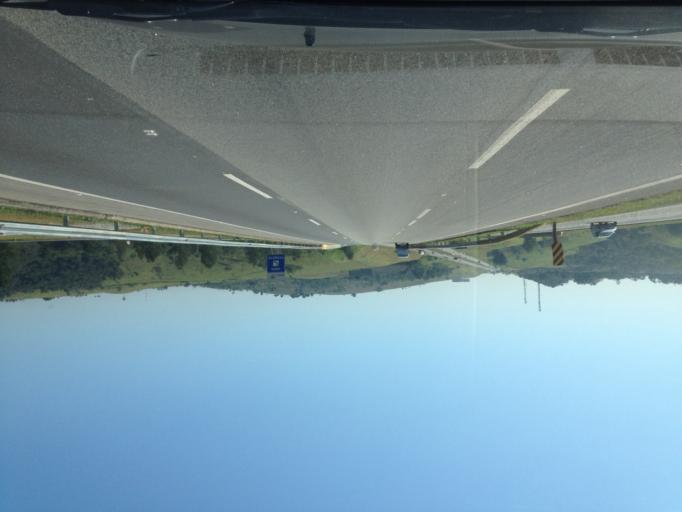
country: BR
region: Sao Paulo
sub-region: Guararema
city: Guararema
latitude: -23.3545
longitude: -46.0564
